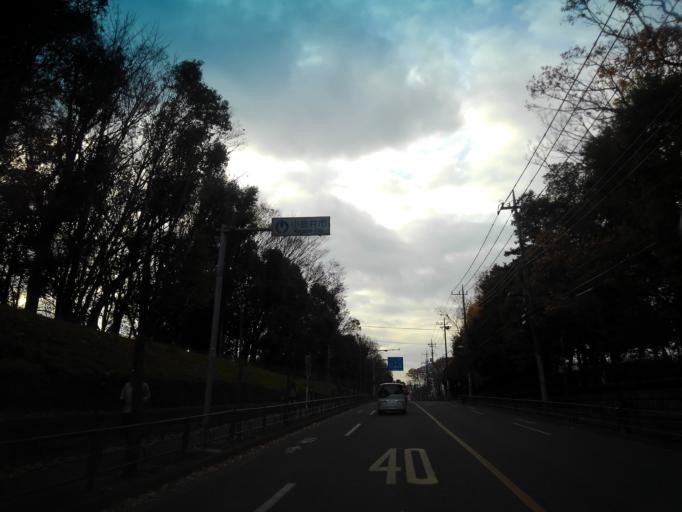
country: JP
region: Tokyo
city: Tanashicho
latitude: 35.7163
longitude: 139.5084
